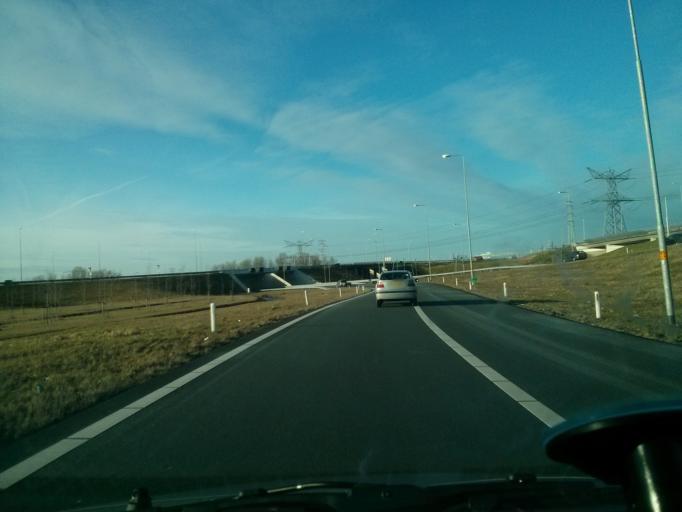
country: NL
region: Gelderland
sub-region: Gemeente Overbetuwe
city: Herveld
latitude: 51.9076
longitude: 5.7709
